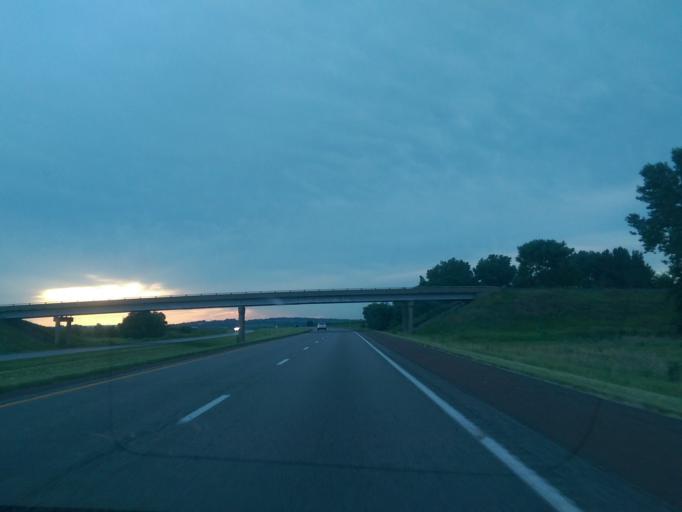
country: US
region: Missouri
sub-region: Holt County
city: Mound City
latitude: 40.1792
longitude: -95.3122
